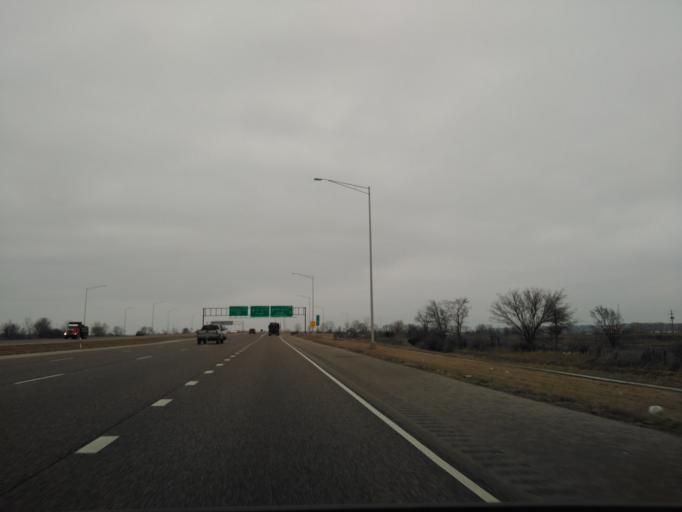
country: US
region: Illinois
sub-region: Saint Clair County
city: Caseyville
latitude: 38.6677
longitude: -90.0291
